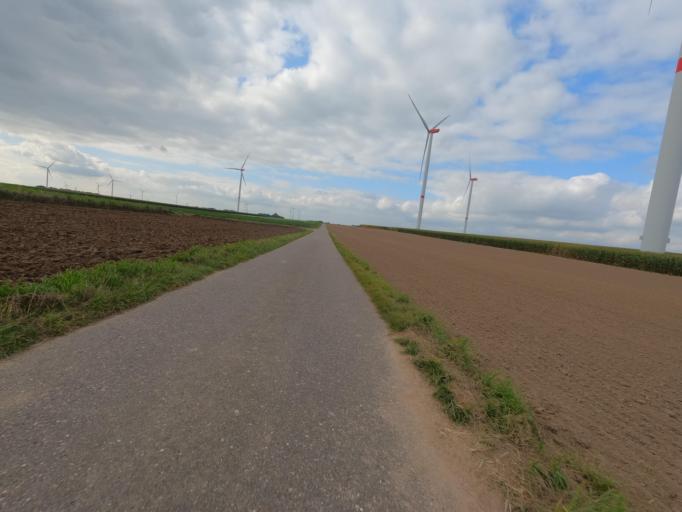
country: DE
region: North Rhine-Westphalia
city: Geilenkirchen
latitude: 51.0126
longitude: 6.1584
